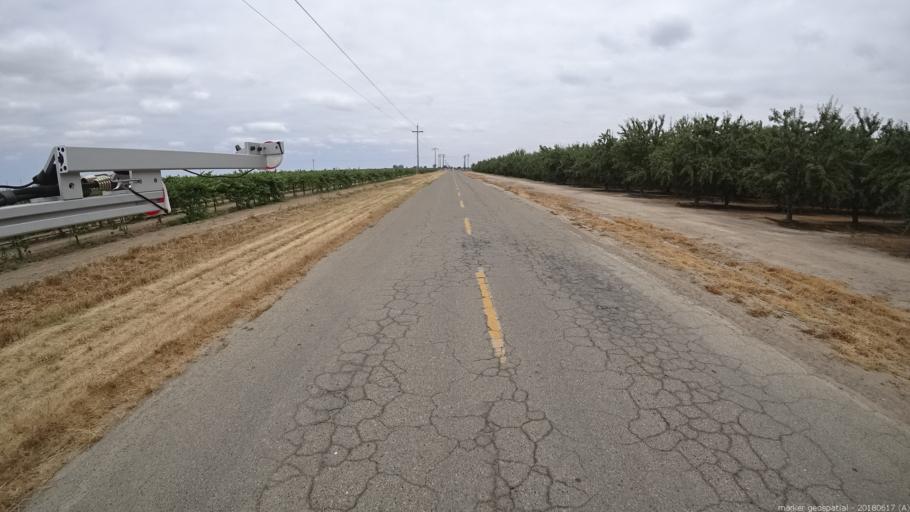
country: US
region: California
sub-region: Madera County
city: Parkwood
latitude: 36.8780
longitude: -120.1649
